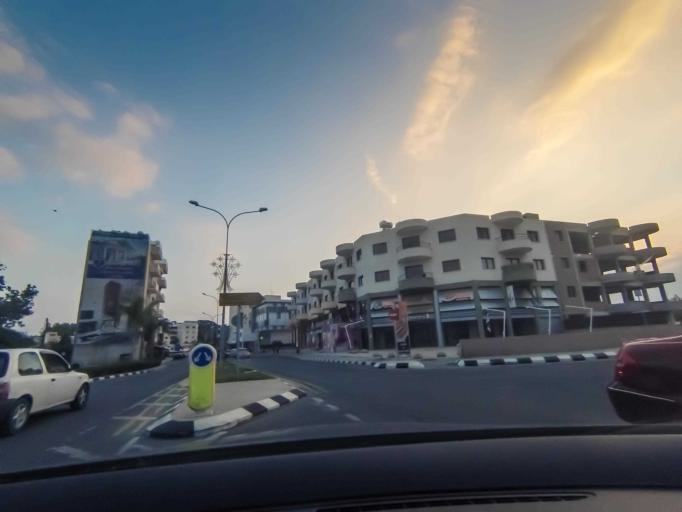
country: CY
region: Limassol
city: Mouttagiaka
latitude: 34.6979
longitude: 33.0884
